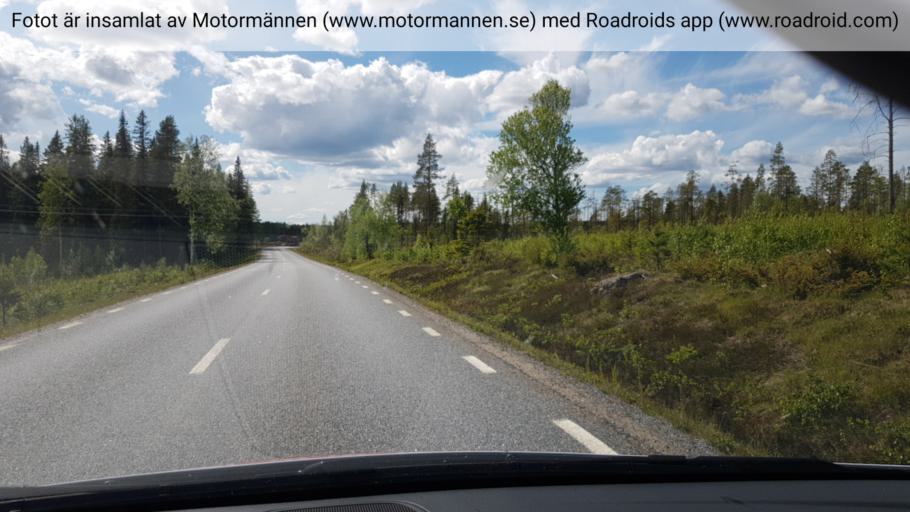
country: SE
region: Vaesterbotten
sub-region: Skelleftea Kommun
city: Burtraesk
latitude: 64.4015
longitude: 20.3569
